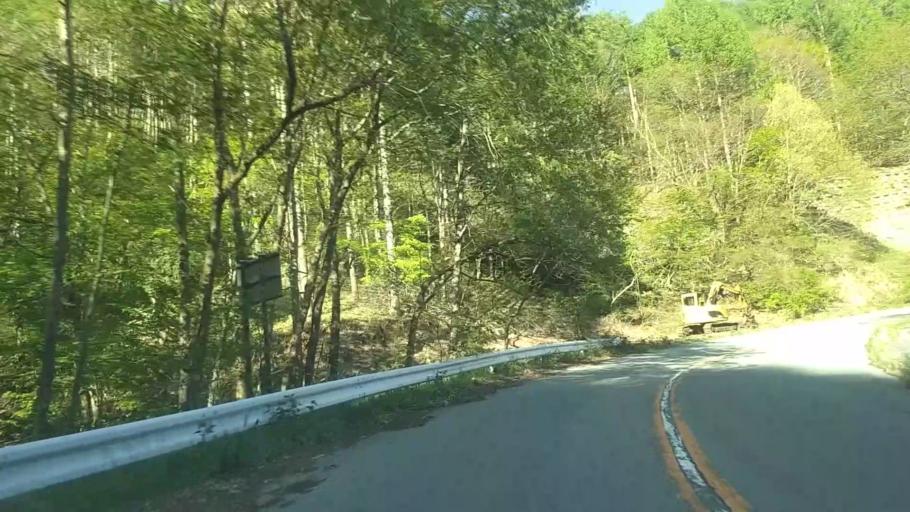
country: JP
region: Yamanashi
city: Nirasaki
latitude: 35.9077
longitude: 138.3894
